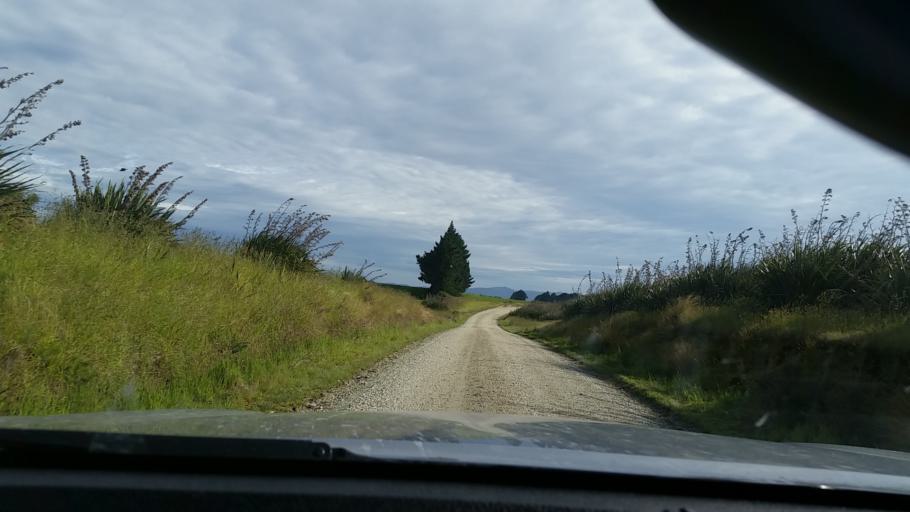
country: NZ
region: Southland
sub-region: Gore District
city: Gore
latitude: -46.2309
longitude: 168.7707
